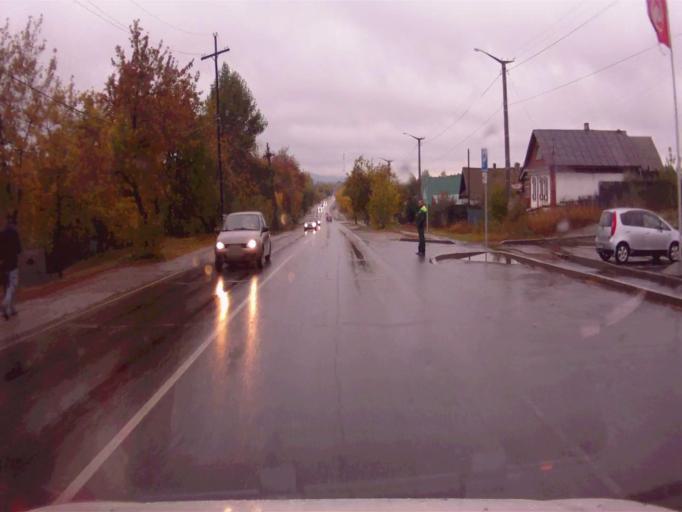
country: RU
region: Chelyabinsk
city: Kyshtym
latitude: 55.7082
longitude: 60.5569
